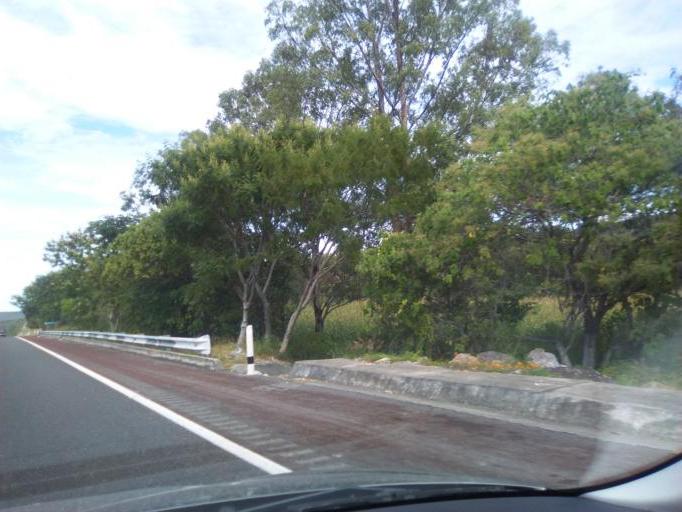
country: MX
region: Guerrero
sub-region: Eduardo Neri
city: Axaxacualco
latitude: 17.8144
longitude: -99.4616
